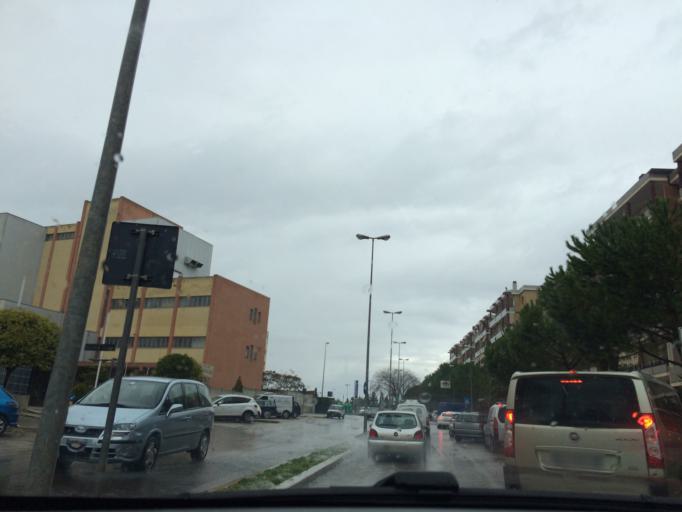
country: IT
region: Basilicate
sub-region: Provincia di Matera
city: Matera
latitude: 40.6777
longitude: 16.5819
